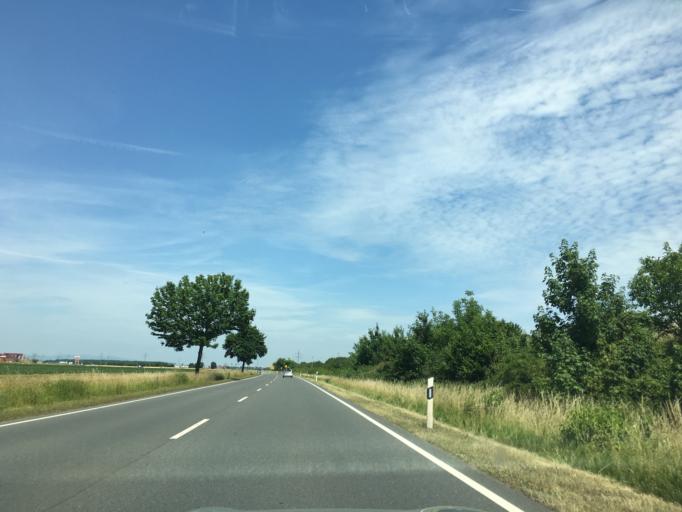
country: DE
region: Hesse
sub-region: Regierungsbezirk Darmstadt
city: Riedstadt
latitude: 49.8301
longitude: 8.4807
